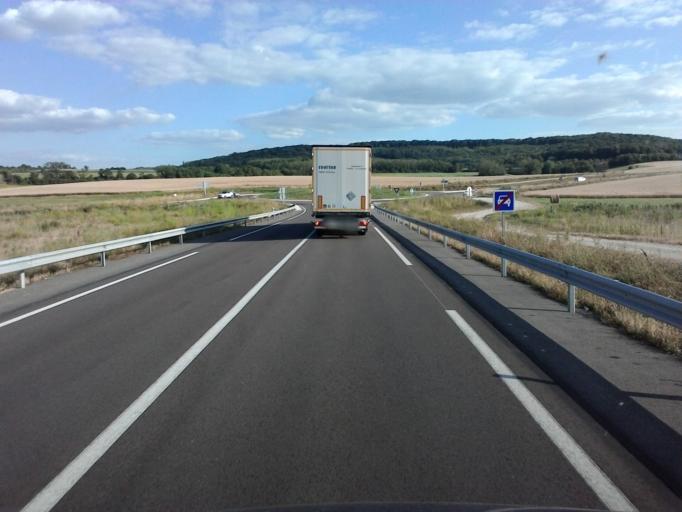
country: FR
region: Franche-Comte
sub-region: Departement de la Haute-Saone
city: Frotey-les-Vesoul
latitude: 47.6880
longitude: 6.2663
